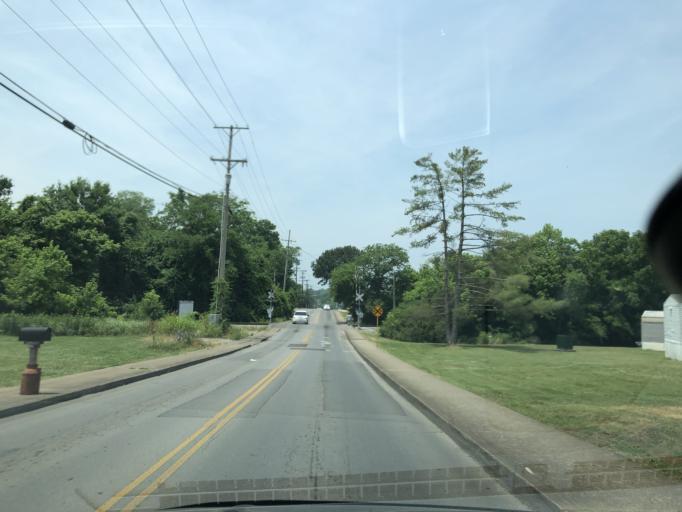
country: US
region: Tennessee
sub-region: Davidson County
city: Oak Hill
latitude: 36.0687
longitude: -86.6764
